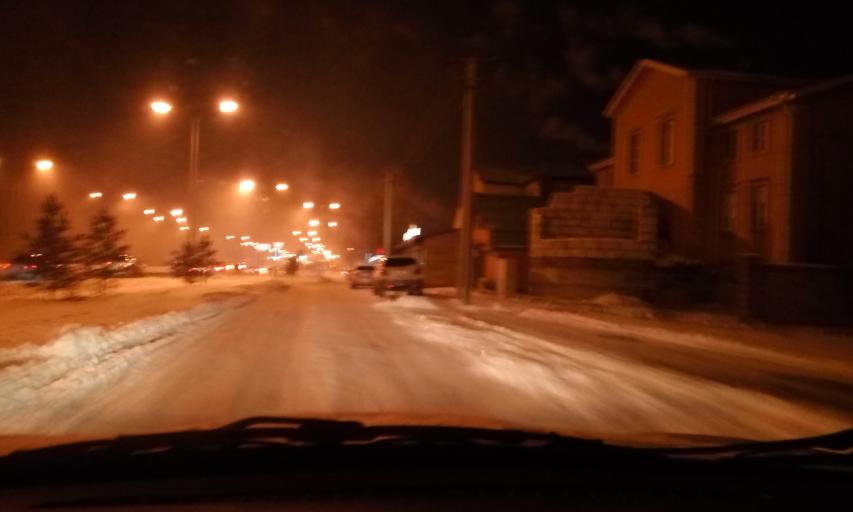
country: KZ
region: Astana Qalasy
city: Astana
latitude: 51.1400
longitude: 71.4890
